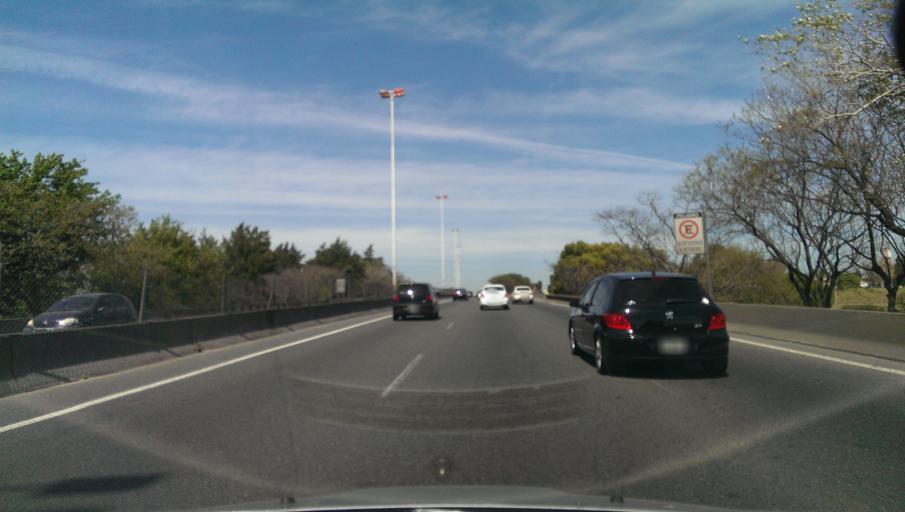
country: AR
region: Buenos Aires F.D.
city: Villa Lugano
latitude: -34.7212
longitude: -58.5128
